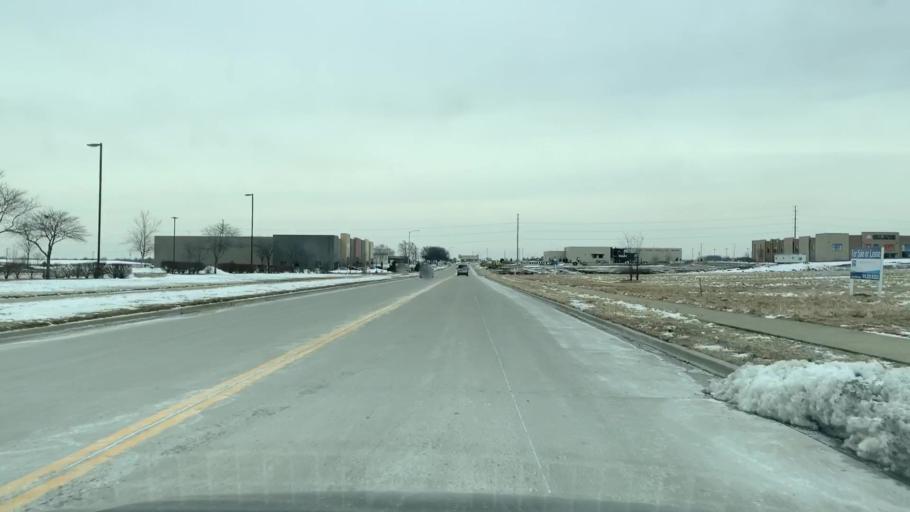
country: US
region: Missouri
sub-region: Jackson County
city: Lees Summit
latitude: 38.9611
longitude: -94.3614
